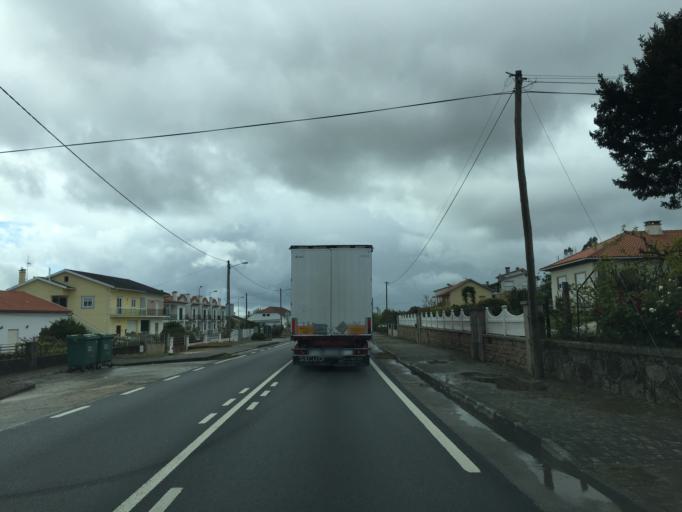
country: PT
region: Coimbra
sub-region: Oliveira do Hospital
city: Oliveira do Hospital
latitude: 40.3153
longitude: -7.9028
